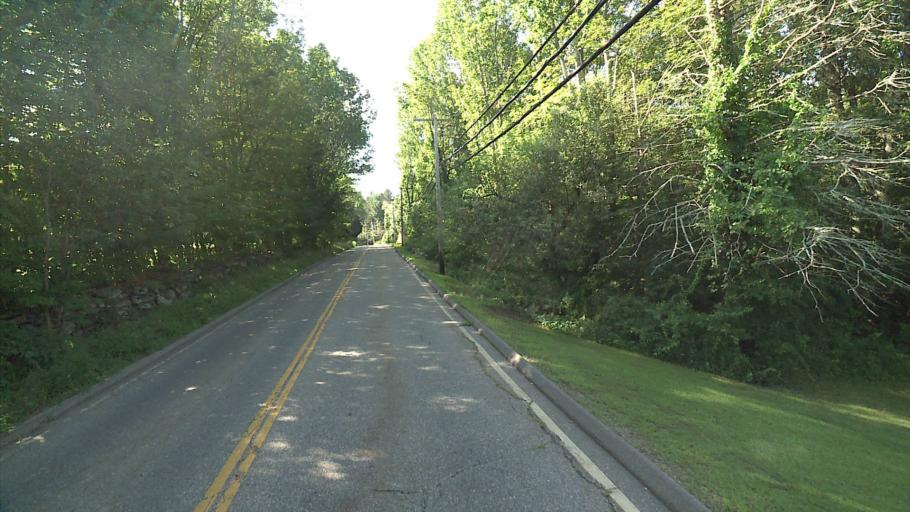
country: US
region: Connecticut
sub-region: New London County
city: Montville Center
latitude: 41.4989
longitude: -72.1982
